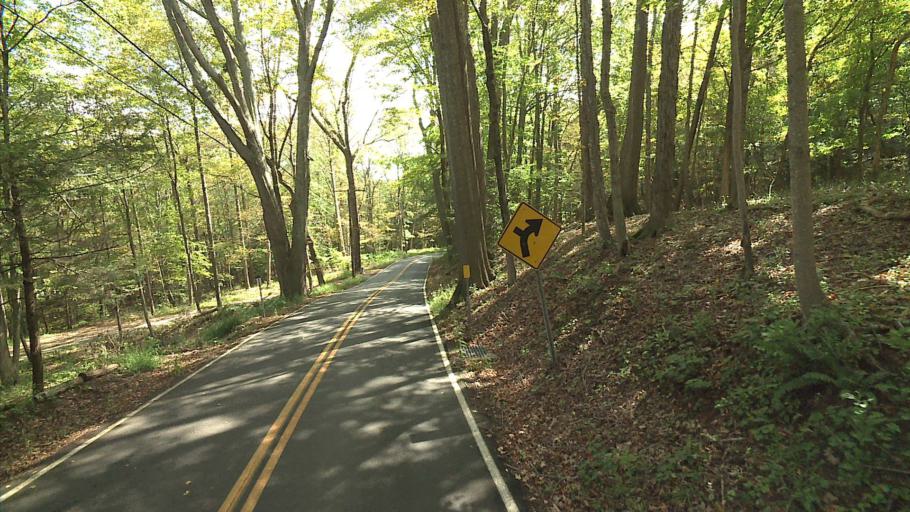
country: US
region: Connecticut
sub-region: Middlesex County
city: Chester Center
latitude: 41.4283
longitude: -72.4239
